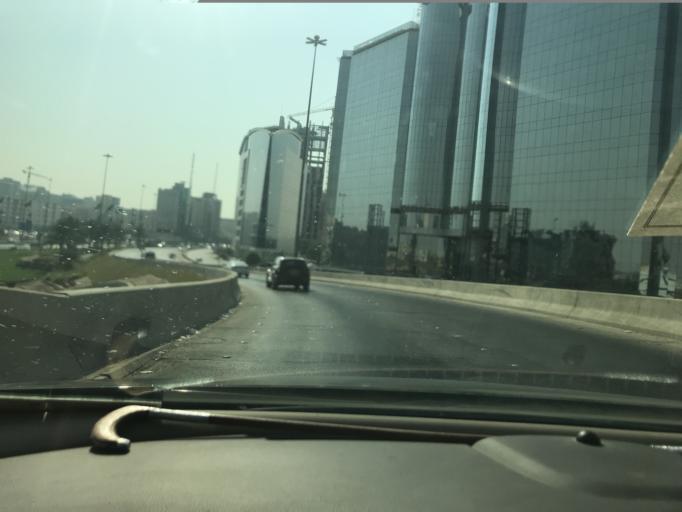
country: SA
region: Ar Riyad
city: Riyadh
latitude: 24.6779
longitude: 46.6875
